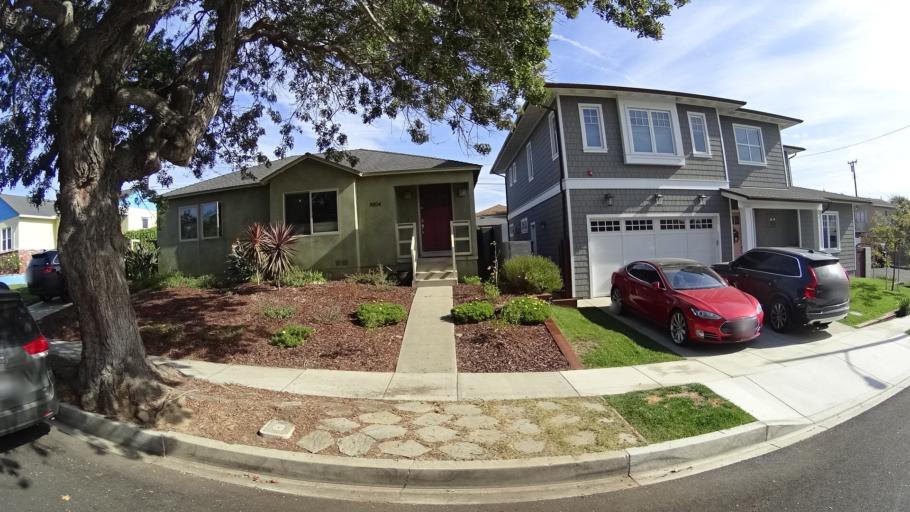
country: US
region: California
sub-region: Los Angeles County
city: Del Aire
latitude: 33.8922
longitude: -118.3826
